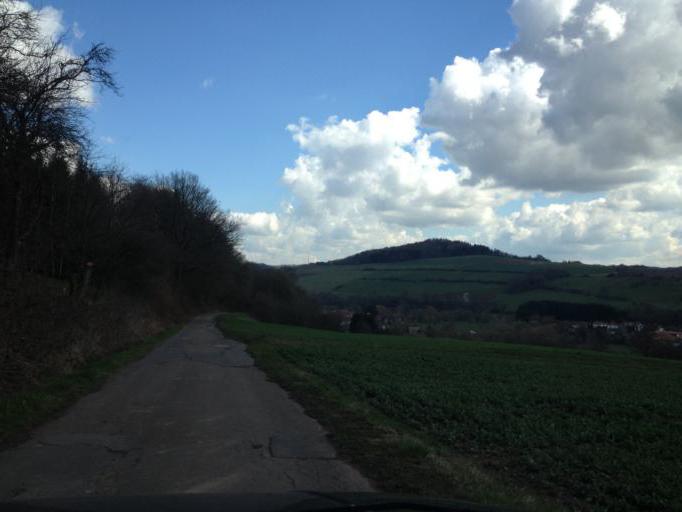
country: DE
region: Rheinland-Pfalz
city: Breitenbach
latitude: 49.4472
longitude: 7.2223
